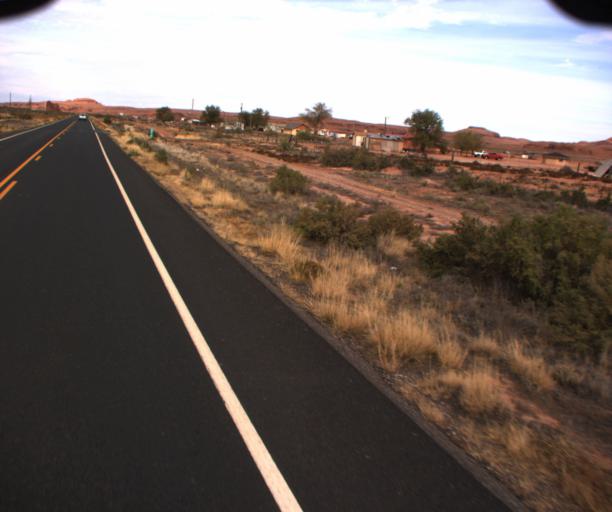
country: US
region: Arizona
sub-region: Apache County
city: Many Farms
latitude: 36.7291
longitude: -109.6312
